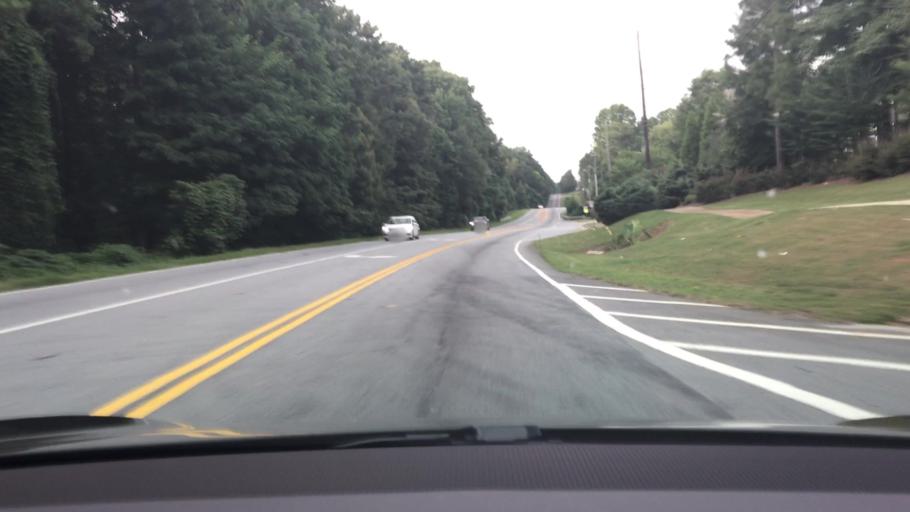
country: US
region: Georgia
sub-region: Gwinnett County
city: Duluth
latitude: 34.0118
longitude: -84.1290
